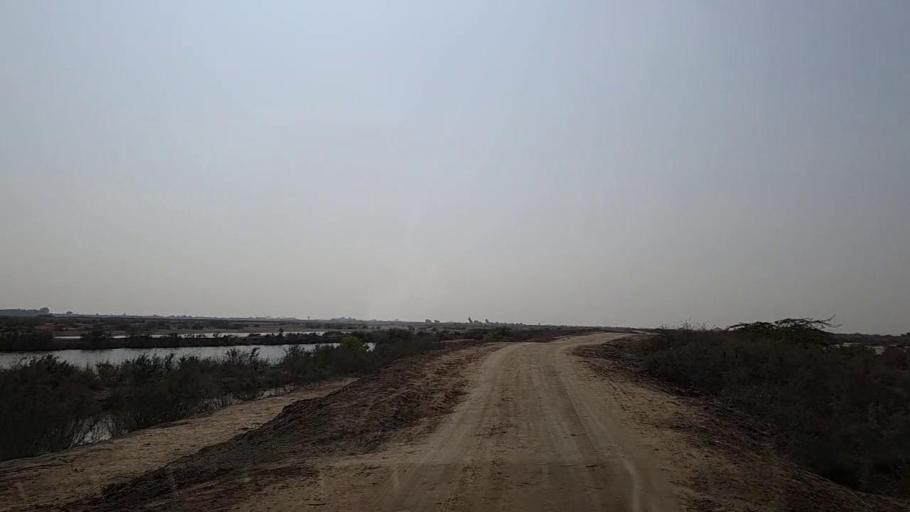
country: PK
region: Sindh
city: Gharo
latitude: 24.6769
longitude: 67.7327
